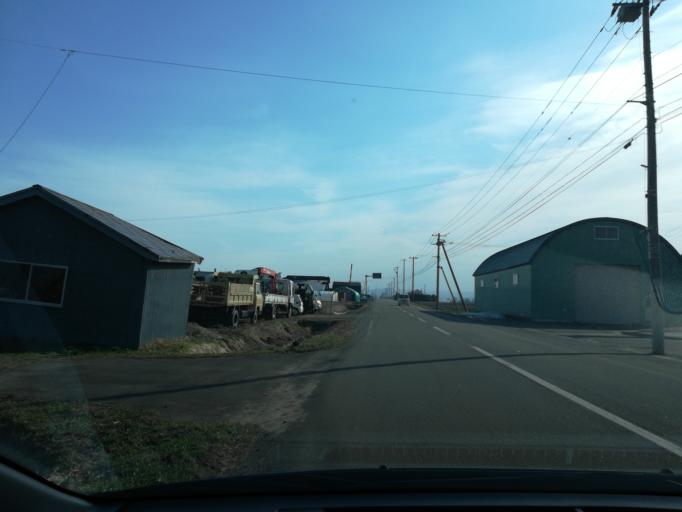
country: JP
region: Hokkaido
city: Iwamizawa
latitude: 43.1632
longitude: 141.6538
